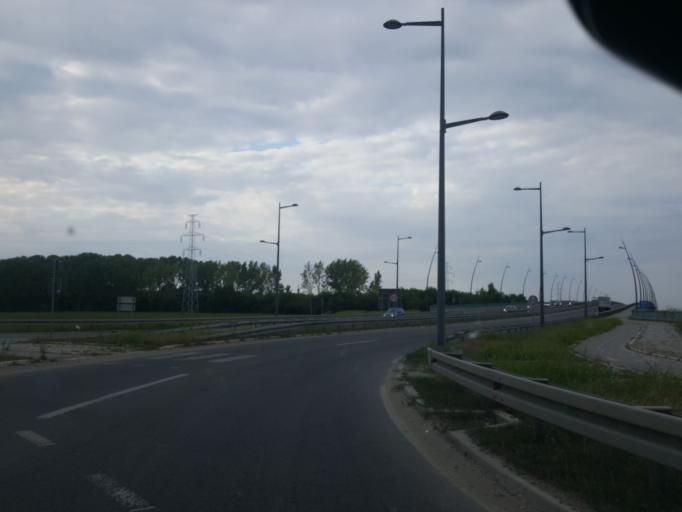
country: RS
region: Autonomna Pokrajina Vojvodina
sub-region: Juznobacki Okrug
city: Novi Sad
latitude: 45.2809
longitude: 19.8032
